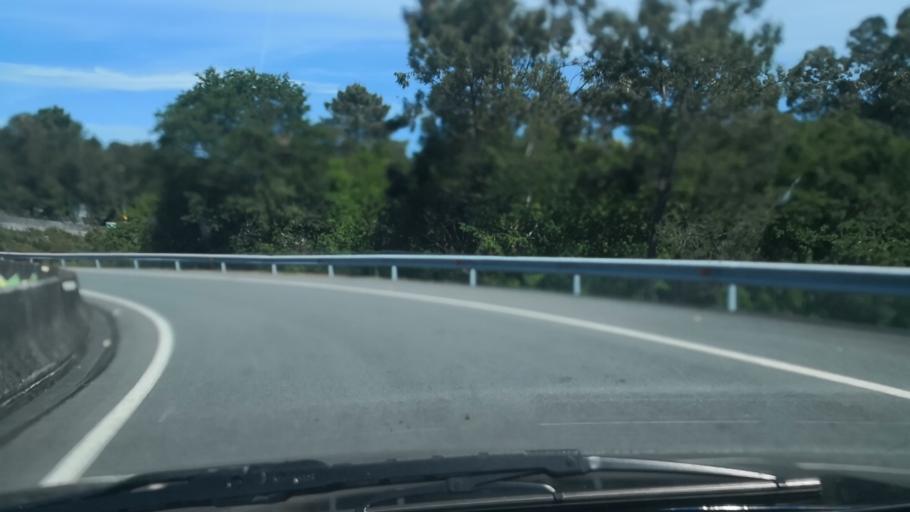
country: ES
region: Galicia
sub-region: Provincia da Coruna
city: Santiago de Compostela
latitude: 42.8094
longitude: -8.5858
